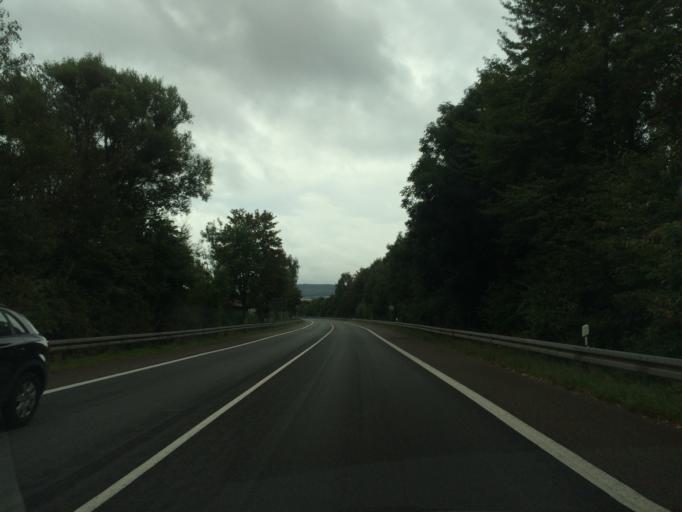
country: DE
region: Saarland
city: Merzig
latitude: 49.4373
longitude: 6.6302
